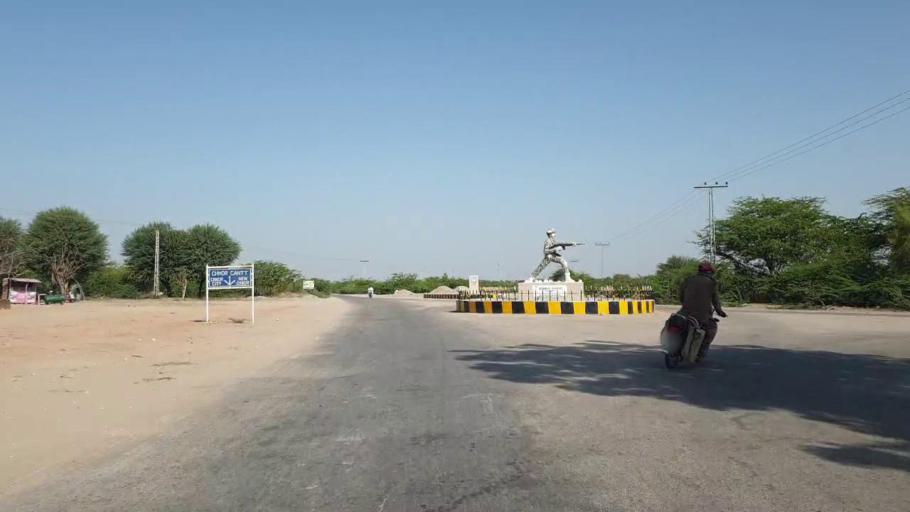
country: PK
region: Sindh
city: Chor
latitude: 25.4898
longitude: 69.7814
